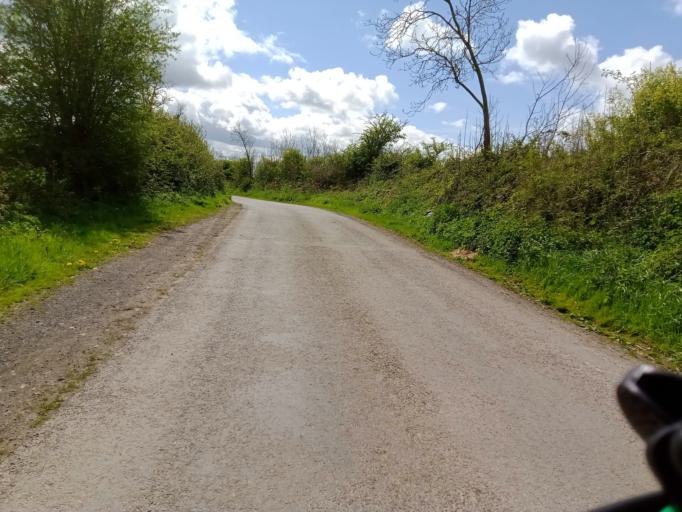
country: IE
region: Leinster
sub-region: Kilkenny
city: Thomastown
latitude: 52.5877
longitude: -7.1446
